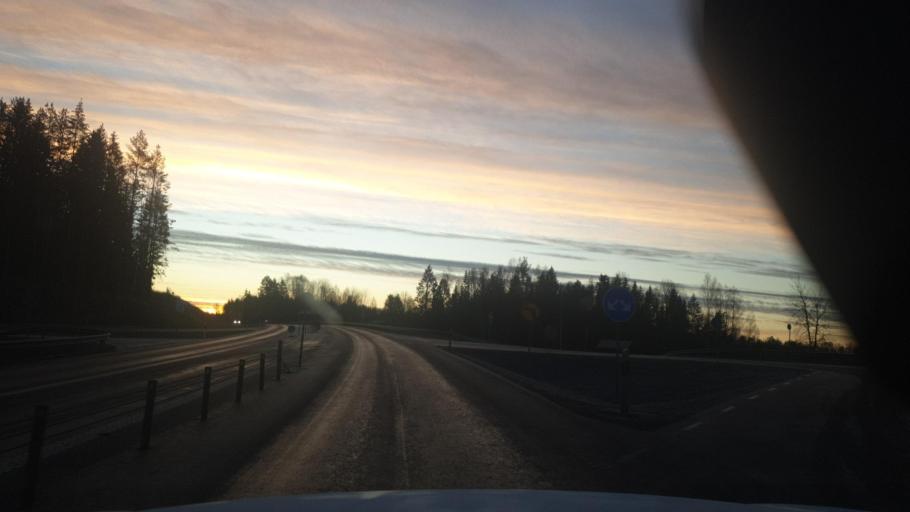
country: SE
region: Vaermland
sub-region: Arvika Kommun
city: Arvika
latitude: 59.6961
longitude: 12.5815
